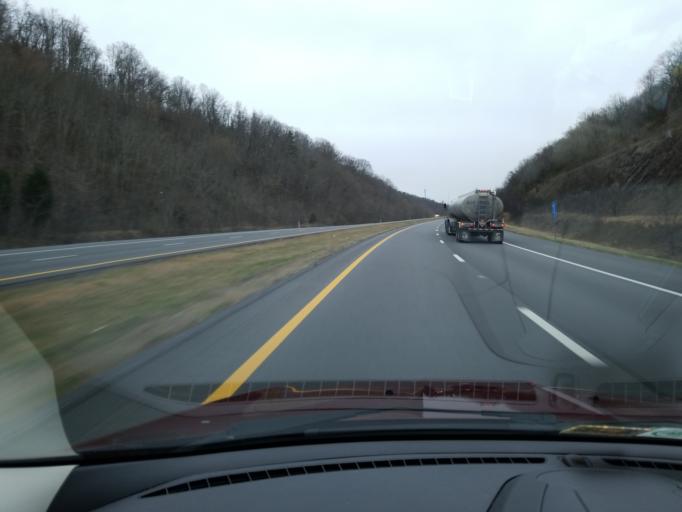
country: US
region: Virginia
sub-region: Giles County
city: Narrows
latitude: 37.3637
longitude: -80.8720
